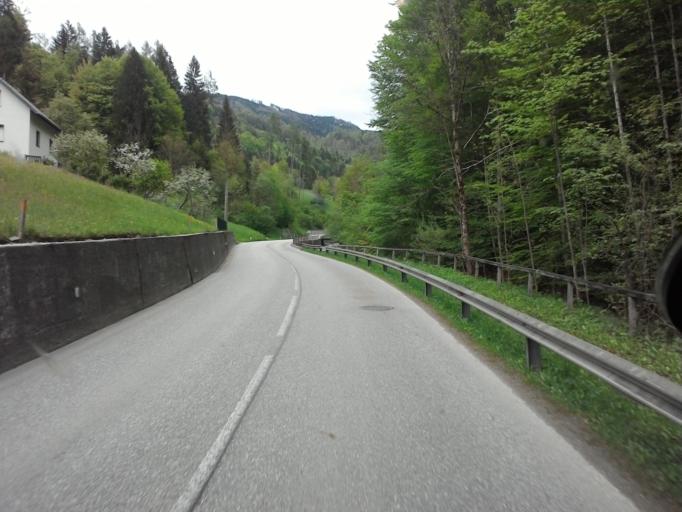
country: AT
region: Upper Austria
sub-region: Politischer Bezirk Kirchdorf an der Krems
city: Rossleithen
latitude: 47.7193
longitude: 14.3597
